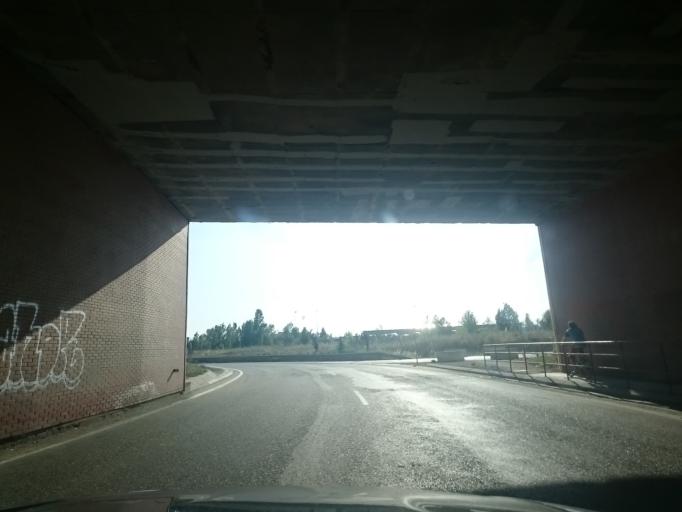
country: ES
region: Castille and Leon
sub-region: Provincia de Burgos
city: Cardenajimeno
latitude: 42.3452
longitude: -3.6379
